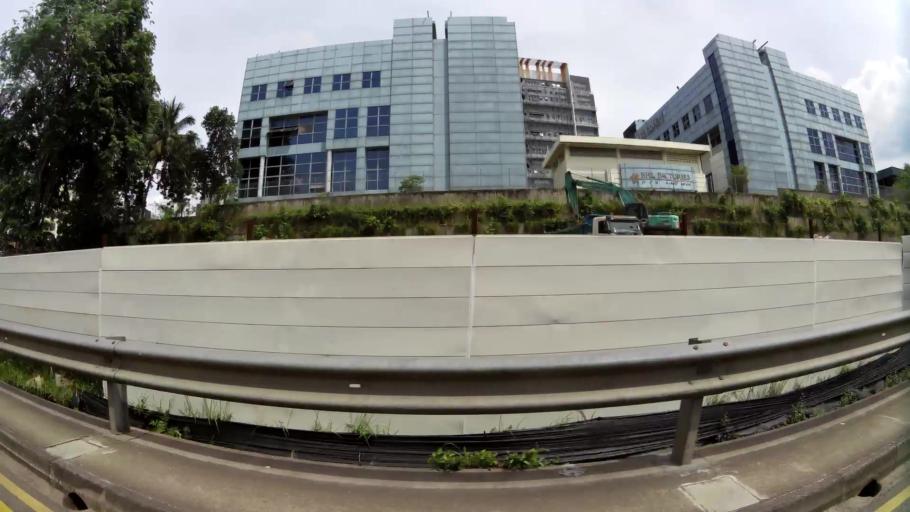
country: MY
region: Johor
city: Johor Bahru
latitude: 1.4065
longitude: 103.7562
